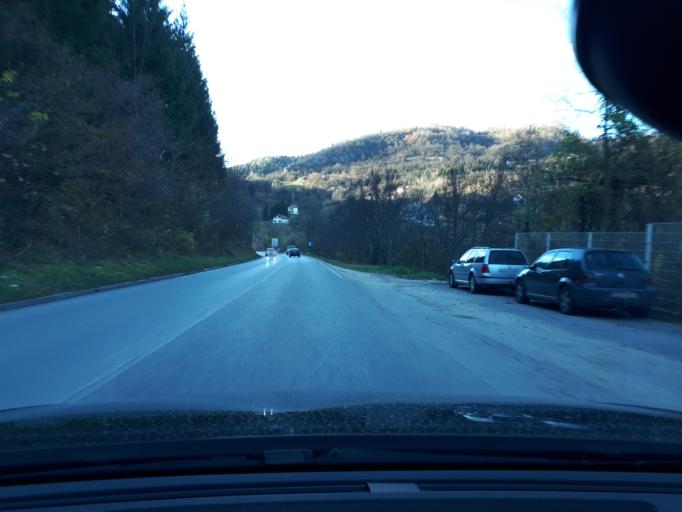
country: BA
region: Republika Srpska
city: Pale
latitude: 43.8497
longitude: 18.5435
